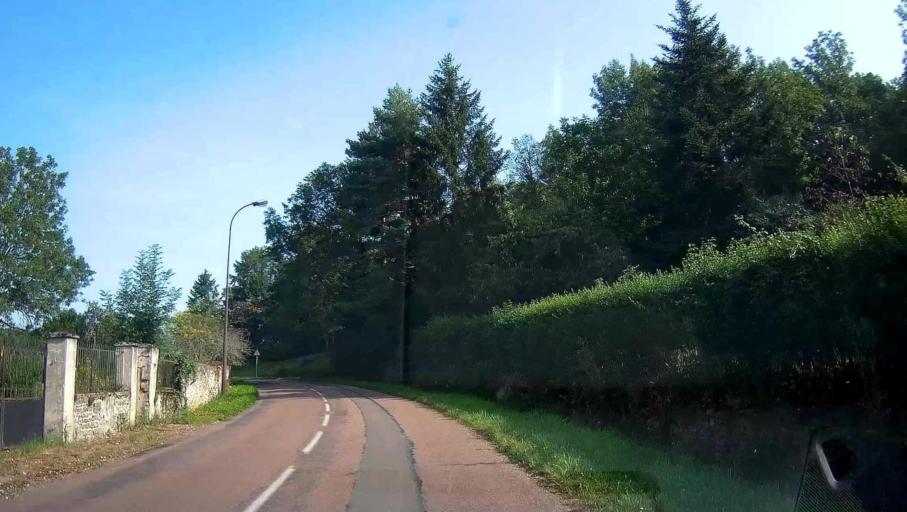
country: FR
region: Bourgogne
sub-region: Departement de Saone-et-Loire
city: Couches
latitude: 46.9014
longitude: 4.5966
